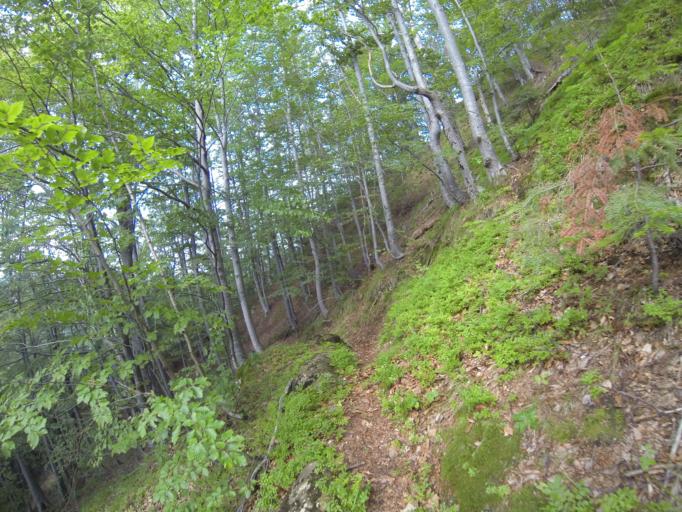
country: RO
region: Valcea
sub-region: Comuna Barbatesti
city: Barbatesti
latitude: 45.2536
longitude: 24.1570
